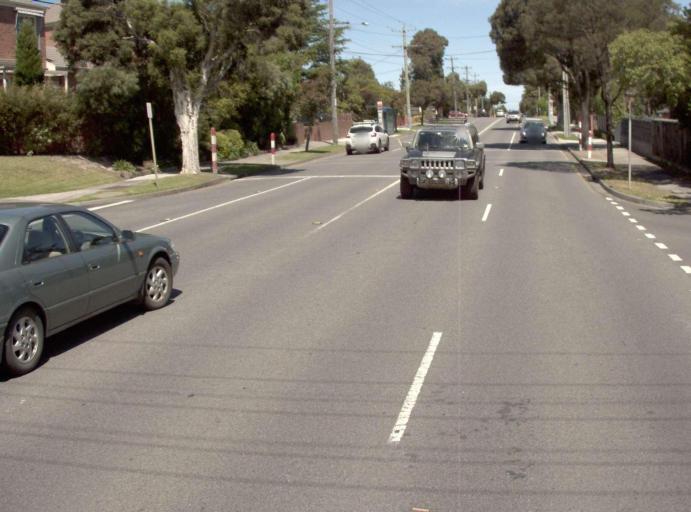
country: AU
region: Victoria
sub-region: Manningham
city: Doncaster East
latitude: -37.7910
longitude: 145.1616
